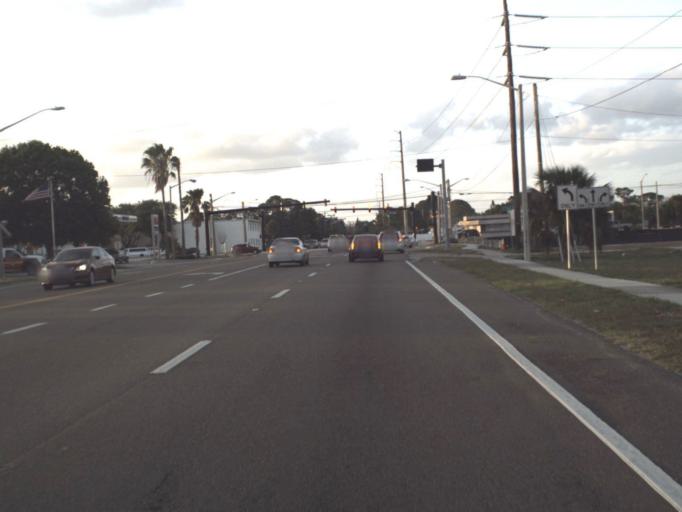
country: US
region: Florida
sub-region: Brevard County
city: Rockledge
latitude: 28.3543
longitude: -80.7425
